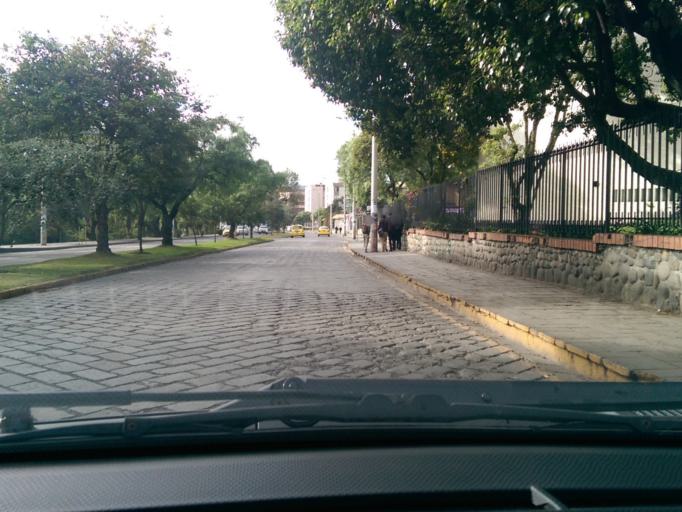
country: EC
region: Azuay
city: Cuenca
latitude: -2.9004
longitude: -79.0086
